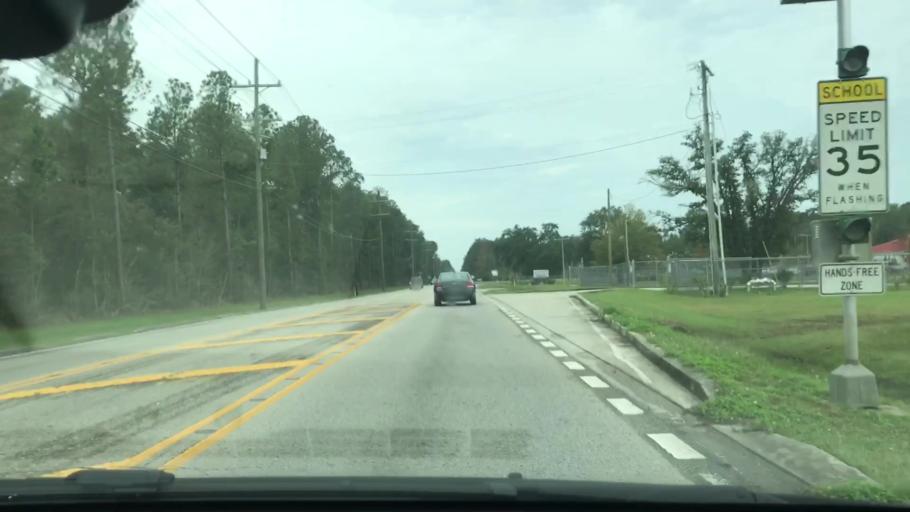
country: US
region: Louisiana
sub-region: Saint Tammany Parish
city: Pearl River
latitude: 30.3574
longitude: -89.7520
